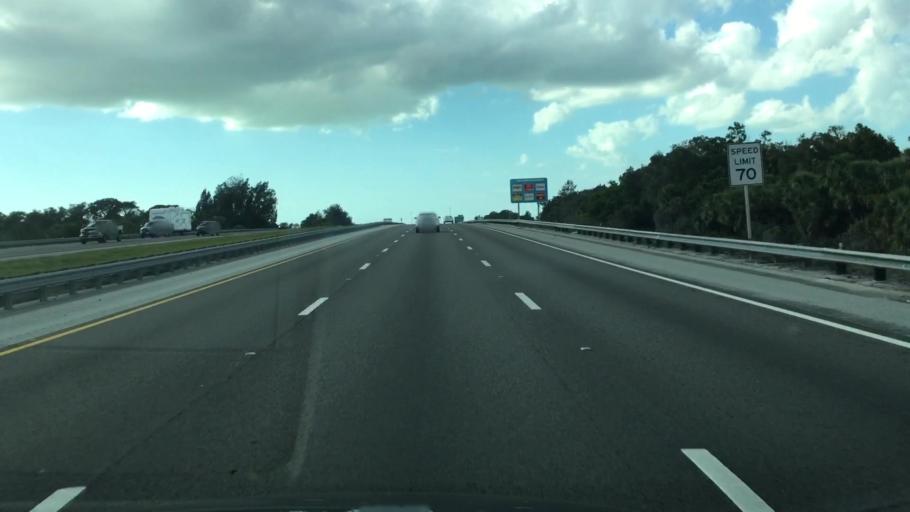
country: US
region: Florida
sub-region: Sarasota County
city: Plantation
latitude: 27.1087
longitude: -82.3655
